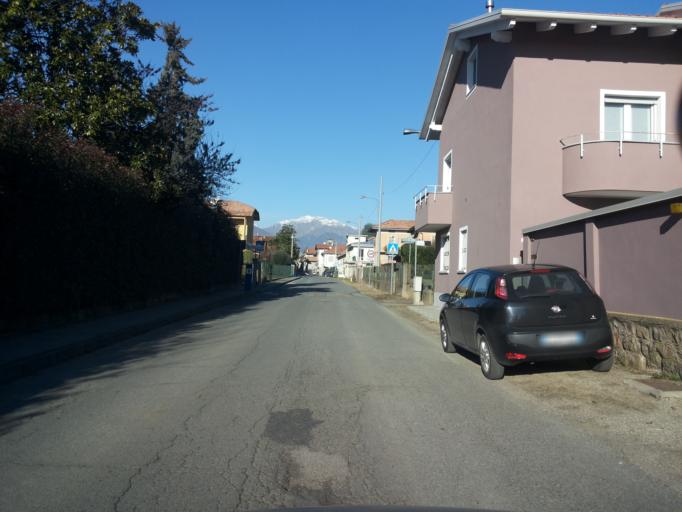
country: IT
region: Piedmont
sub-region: Provincia di Biella
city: Ponderano
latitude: 45.5334
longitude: 8.0564
